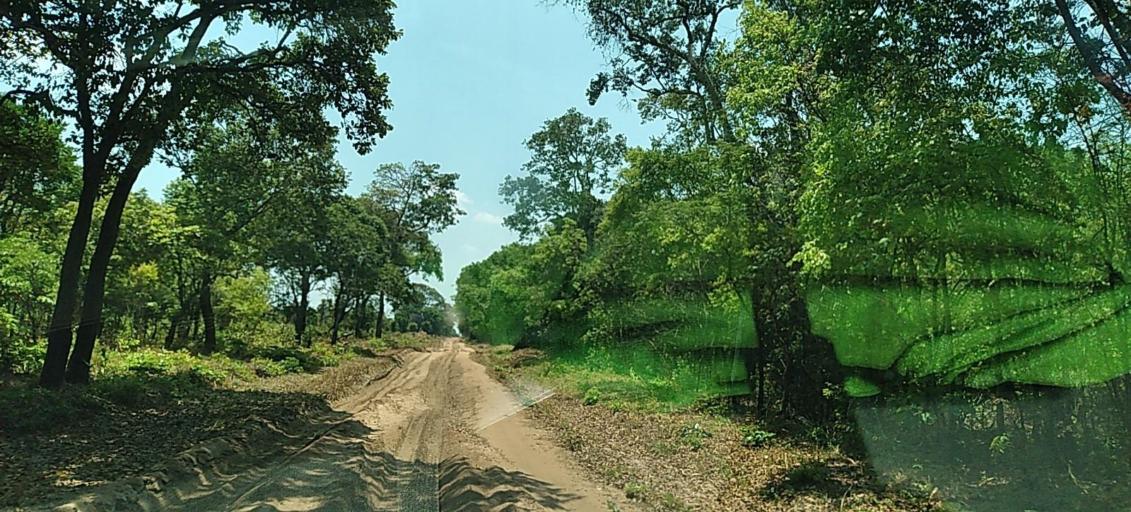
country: CD
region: Katanga
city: Kolwezi
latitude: -11.3911
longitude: 25.2220
